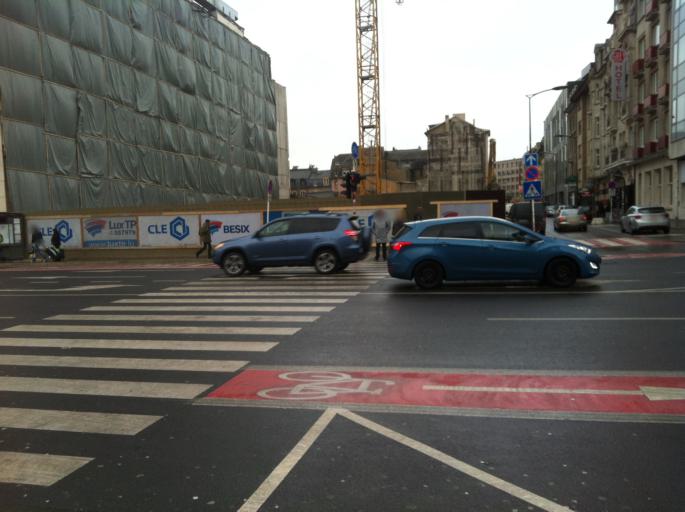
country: LU
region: Luxembourg
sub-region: Canton de Luxembourg
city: Luxembourg
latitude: 49.6000
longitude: 6.1335
